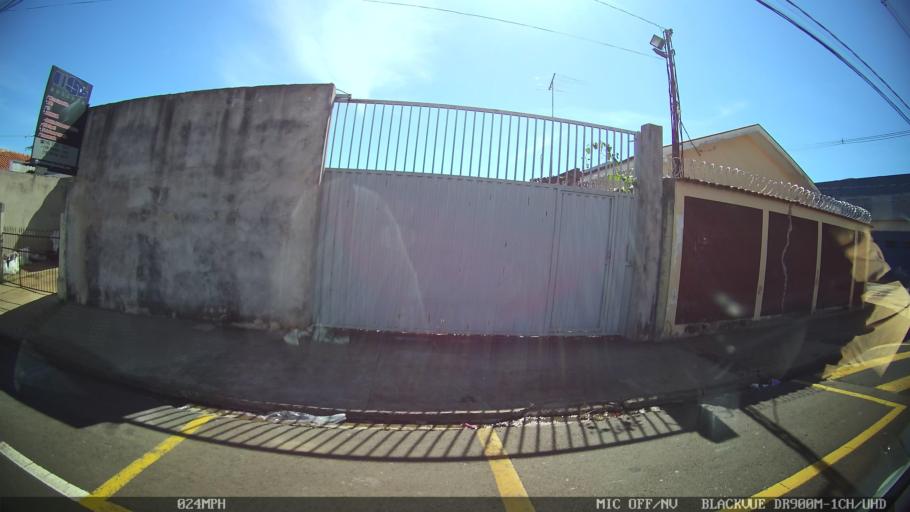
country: BR
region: Sao Paulo
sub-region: Franca
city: Franca
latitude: -20.5469
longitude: -47.3876
